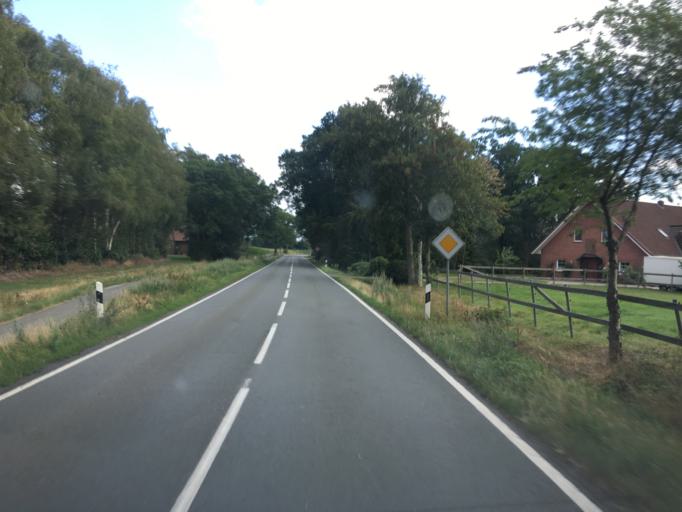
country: DE
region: Lower Saxony
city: Friesoythe
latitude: 53.0569
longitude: 7.8540
